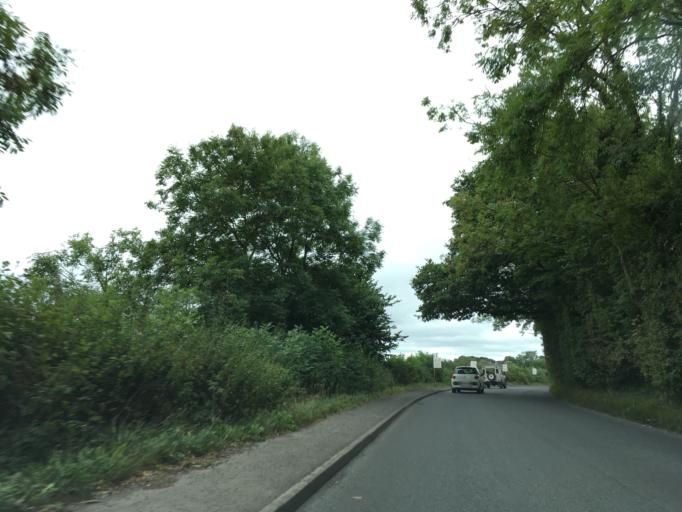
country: GB
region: England
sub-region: Bath and North East Somerset
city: Paulton
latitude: 51.3282
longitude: -2.5104
